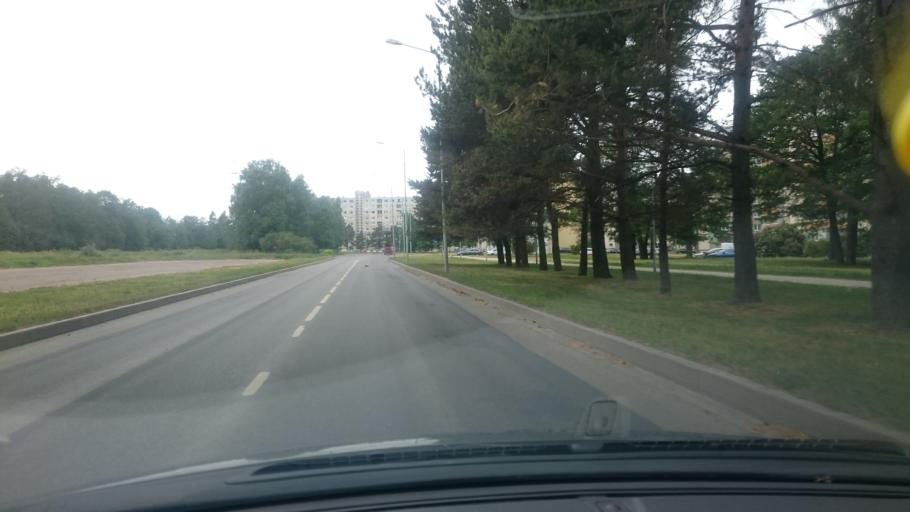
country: EE
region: Harju
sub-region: Saue vald
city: Laagri
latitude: 59.4072
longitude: 24.6378
